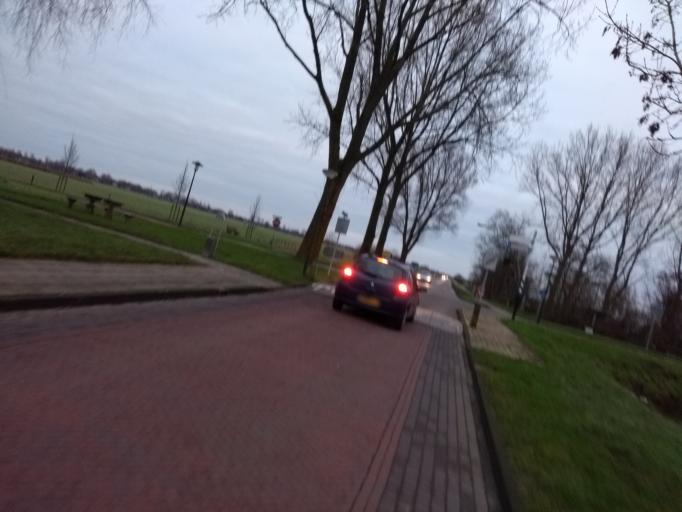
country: NL
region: Friesland
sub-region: Sudwest Fryslan
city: IJlst
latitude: 53.0099
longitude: 5.6326
